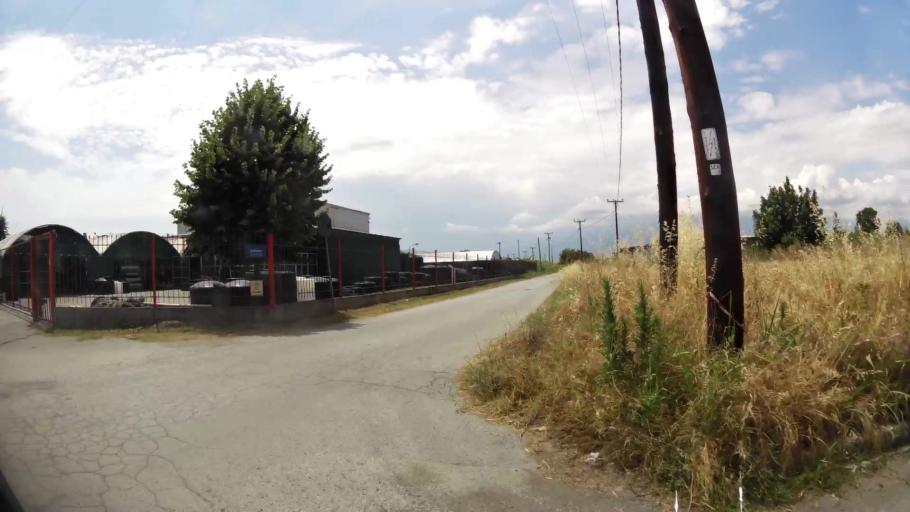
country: GR
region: Central Macedonia
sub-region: Nomos Pierias
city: Katerini
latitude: 40.2584
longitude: 22.5125
